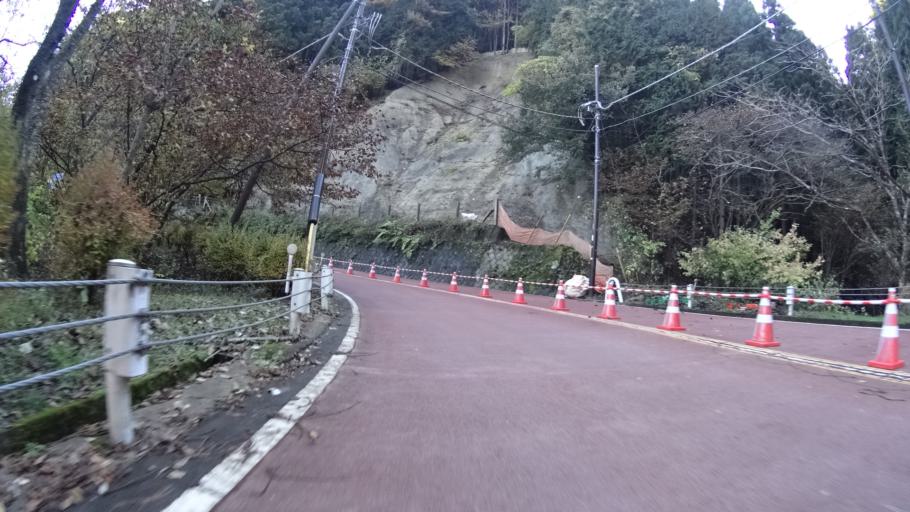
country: JP
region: Yamanashi
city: Uenohara
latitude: 35.7722
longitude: 139.0173
